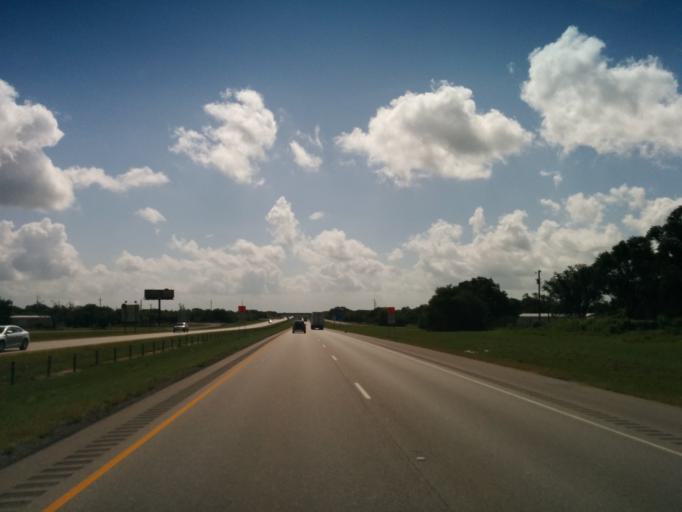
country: US
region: Texas
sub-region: Colorado County
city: Columbus
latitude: 29.6935
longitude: -96.5831
